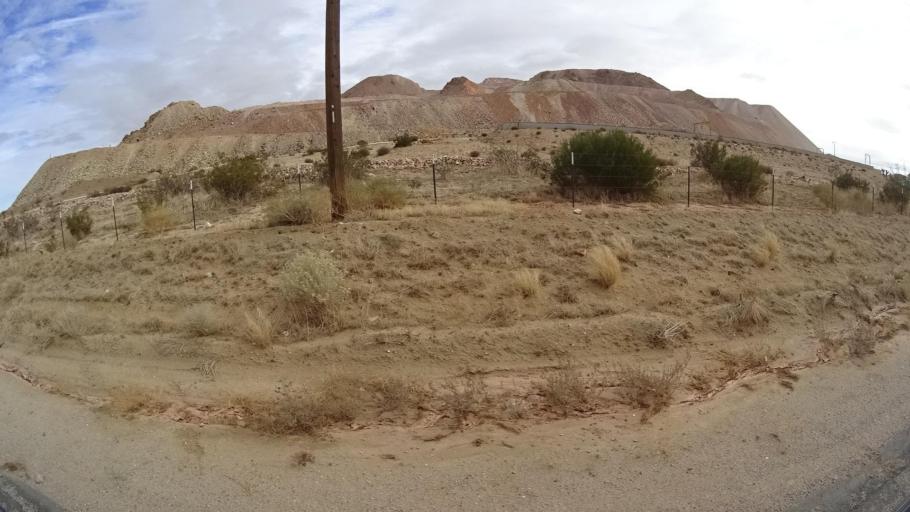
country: US
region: California
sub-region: Kern County
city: Mojave
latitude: 34.9929
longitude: -118.2036
